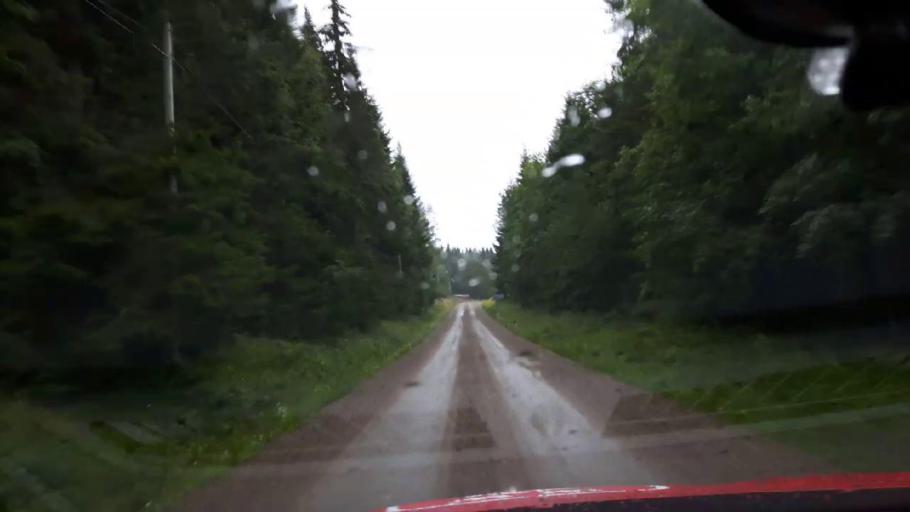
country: SE
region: Jaemtland
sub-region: OEstersunds Kommun
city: Brunflo
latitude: 62.7834
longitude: 14.9710
